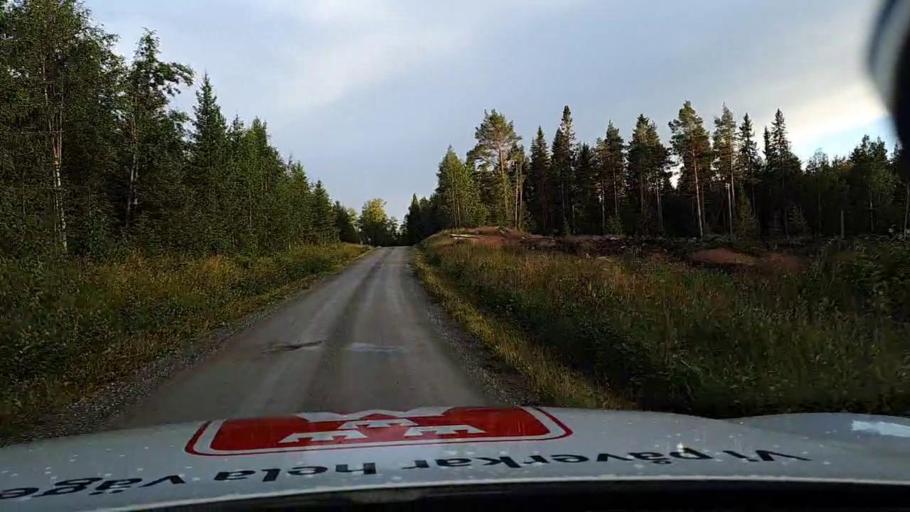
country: SE
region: Jaemtland
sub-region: Bergs Kommun
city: Hoverberg
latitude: 62.8560
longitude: 14.5359
